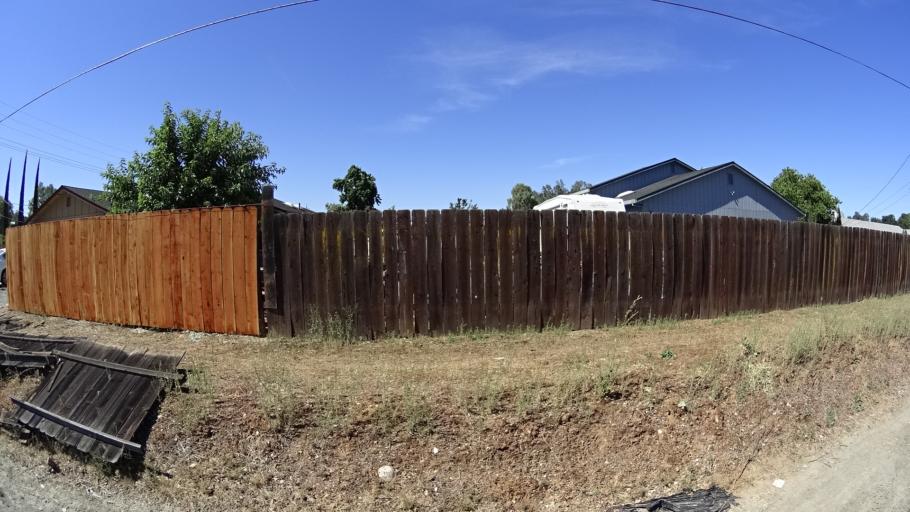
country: US
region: California
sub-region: Calaveras County
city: Rancho Calaveras
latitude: 38.1428
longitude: -120.8640
